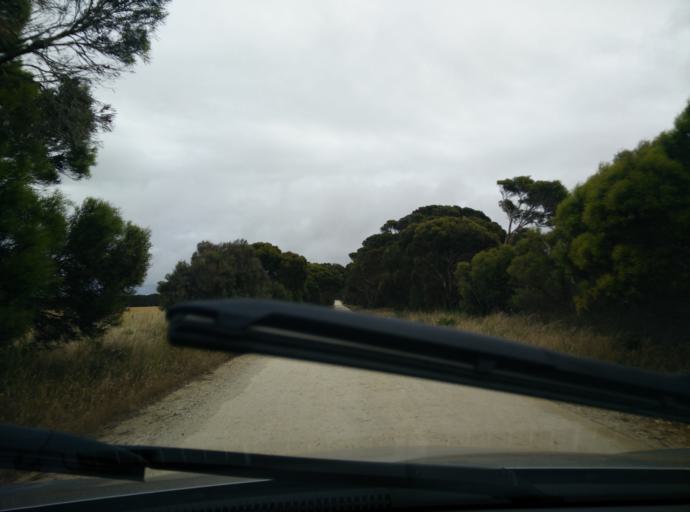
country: AU
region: South Australia
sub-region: Kangaroo Island
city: Kingscote
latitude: -35.8694
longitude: 137.5228
